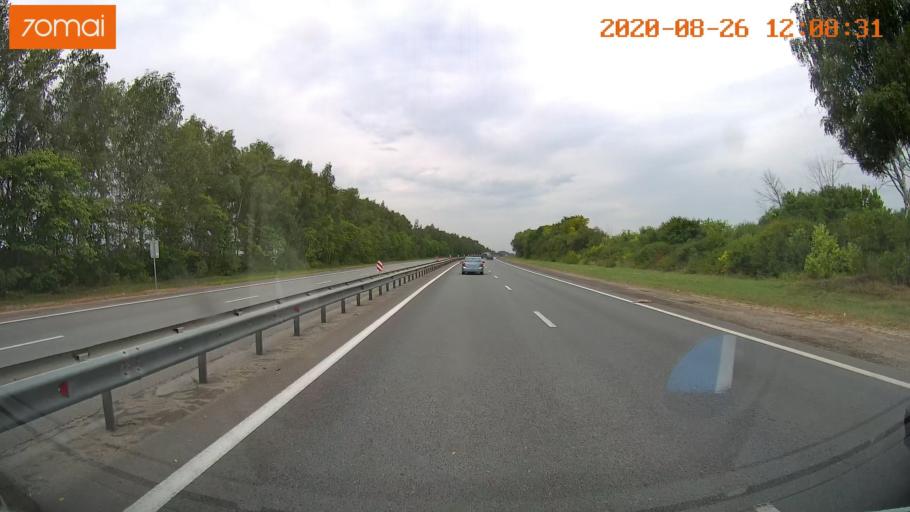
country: RU
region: Rjazan
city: Starozhilovo
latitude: 54.3523
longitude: 40.1183
